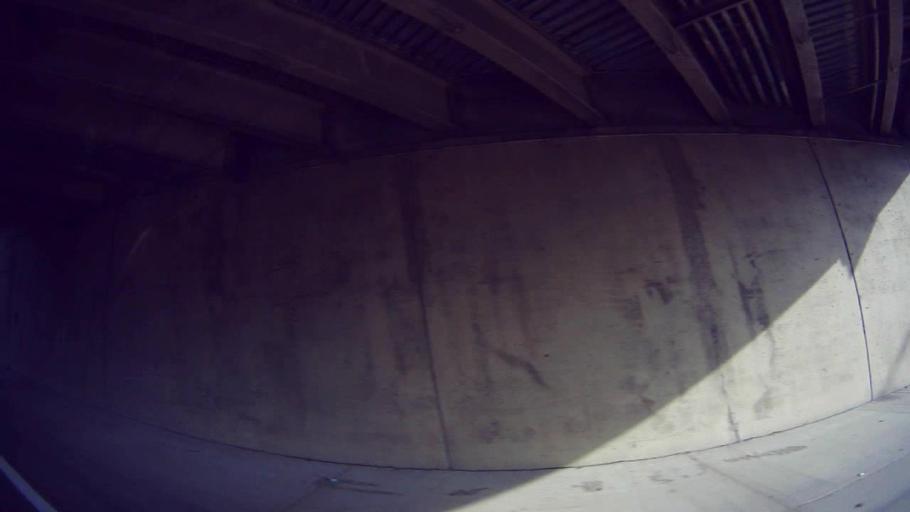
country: US
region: Michigan
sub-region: Oakland County
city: Oak Park
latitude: 42.4377
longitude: -83.1940
